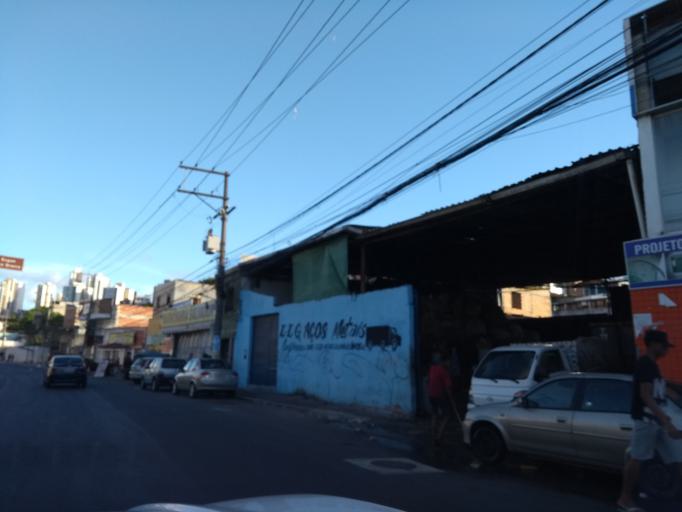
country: BR
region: Bahia
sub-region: Salvador
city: Salvador
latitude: -12.9957
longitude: -38.4963
